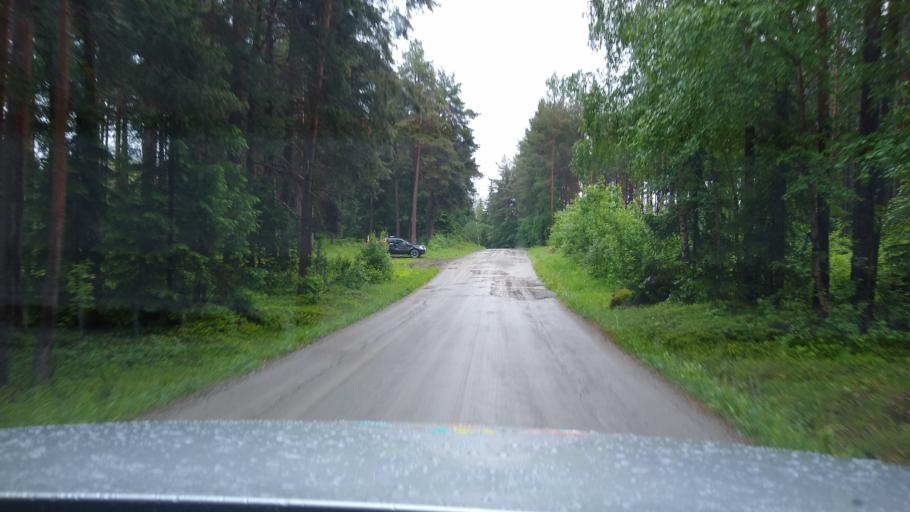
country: NO
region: Oppland
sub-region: Ringebu
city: Ringebu
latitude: 61.5437
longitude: 10.1016
